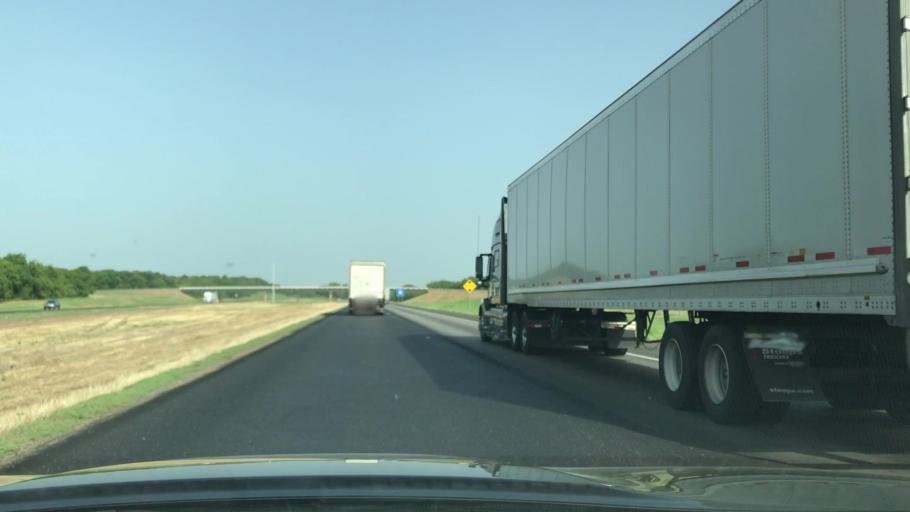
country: US
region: Texas
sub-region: Kaufman County
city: Terrell
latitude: 32.6765
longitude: -96.1765
